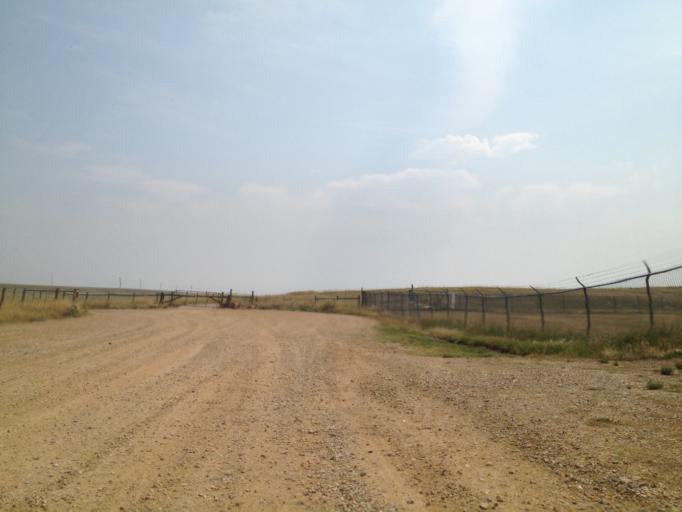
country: US
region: Colorado
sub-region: Boulder County
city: Superior
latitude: 39.9404
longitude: -105.1988
